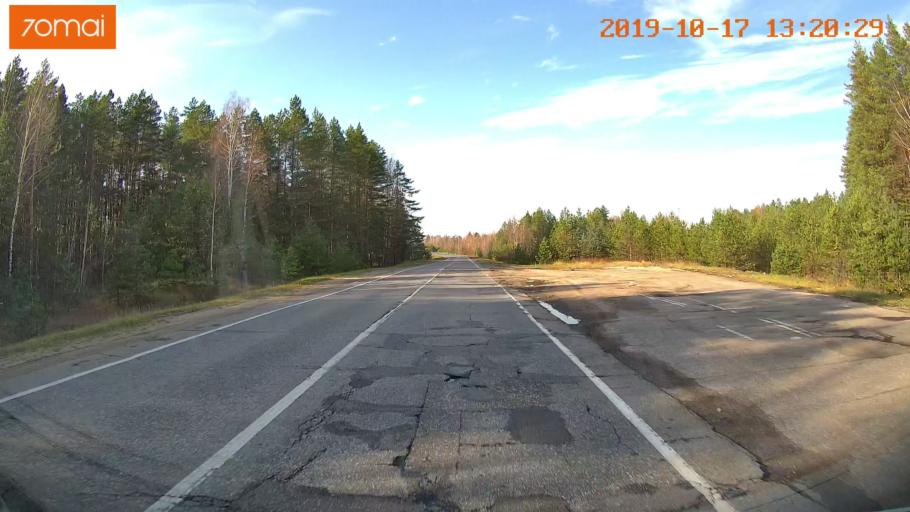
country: RU
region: Rjazan
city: Gus'-Zheleznyy
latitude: 55.0763
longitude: 41.0494
